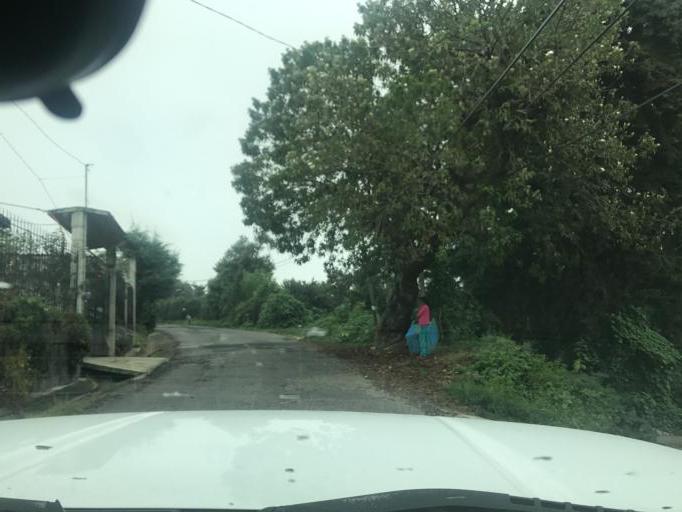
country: MX
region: Morelos
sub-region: Ocuituco
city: Huepalcalco (San Miguel)
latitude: 18.9003
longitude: -98.7529
